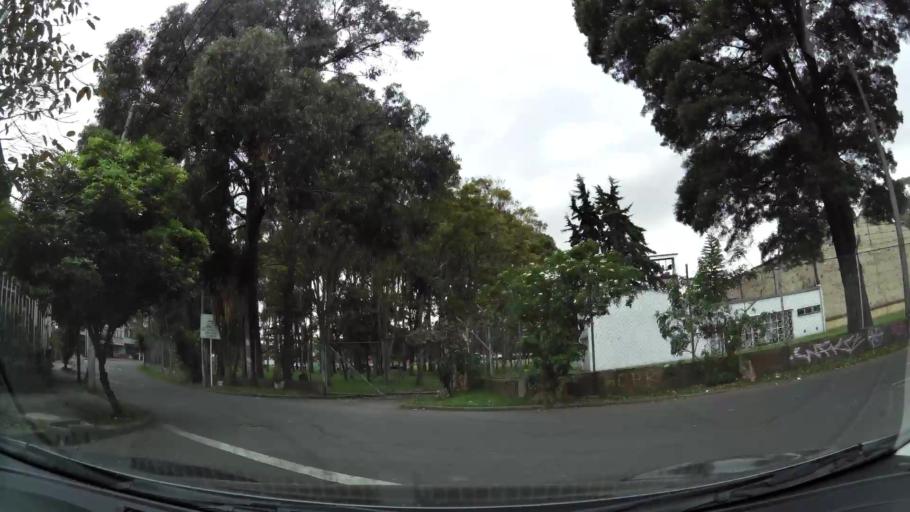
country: CO
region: Bogota D.C.
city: Bogota
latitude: 4.6324
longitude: -74.0815
